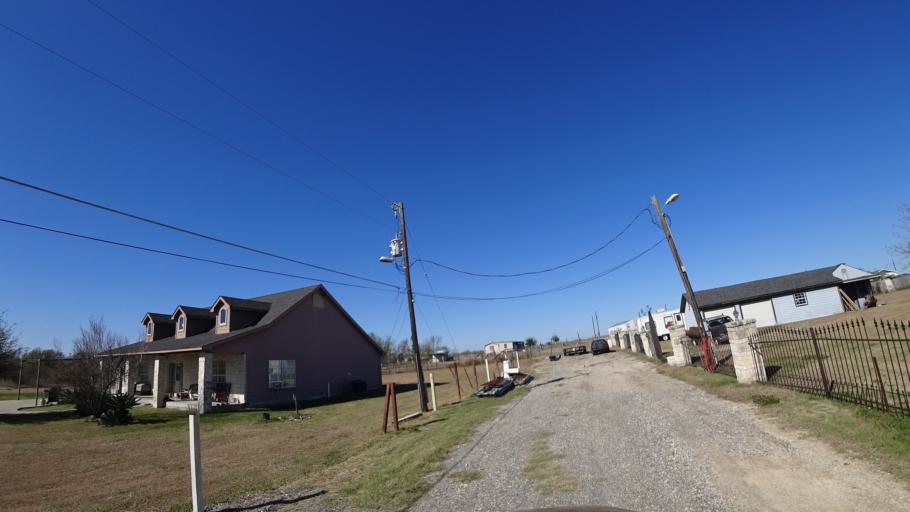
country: US
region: Texas
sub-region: Travis County
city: Garfield
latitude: 30.0990
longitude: -97.6217
